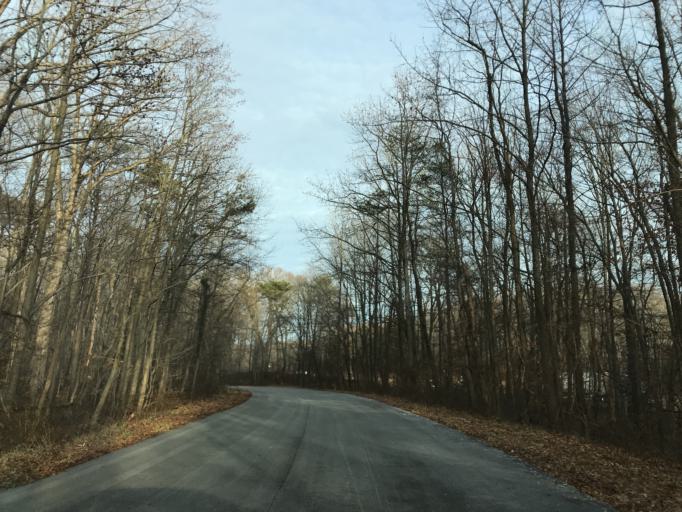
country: US
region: Maryland
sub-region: Baltimore County
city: Kingsville
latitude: 39.4299
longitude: -76.3878
